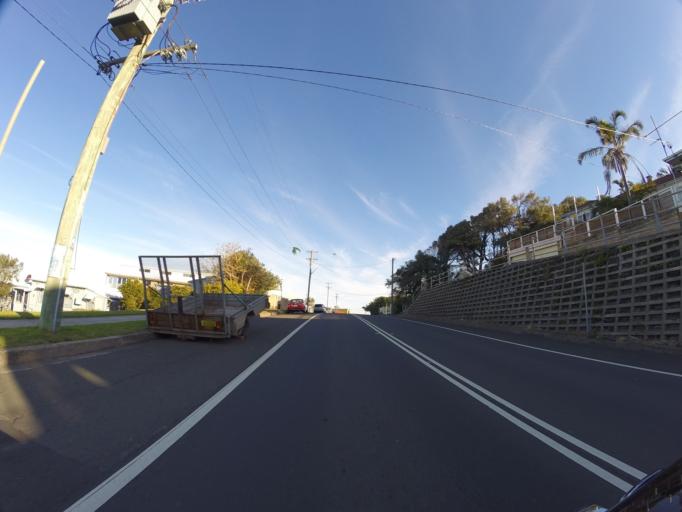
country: AU
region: New South Wales
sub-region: Wollongong
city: Bulli
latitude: -34.3098
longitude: 150.9324
